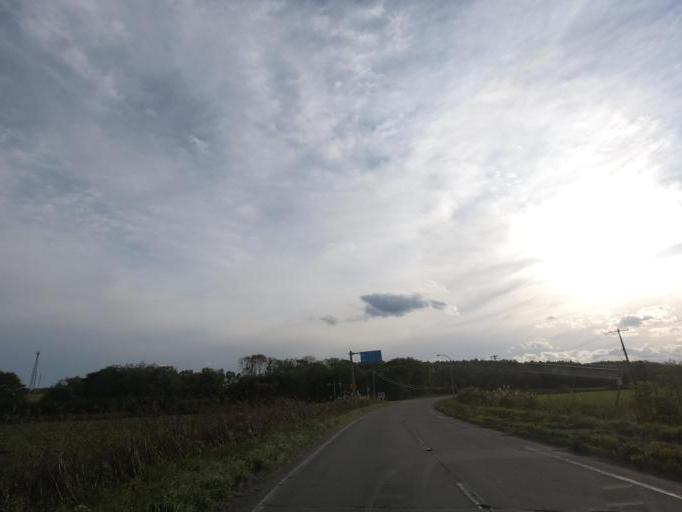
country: JP
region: Hokkaido
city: Obihiro
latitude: 42.5035
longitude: 143.4170
